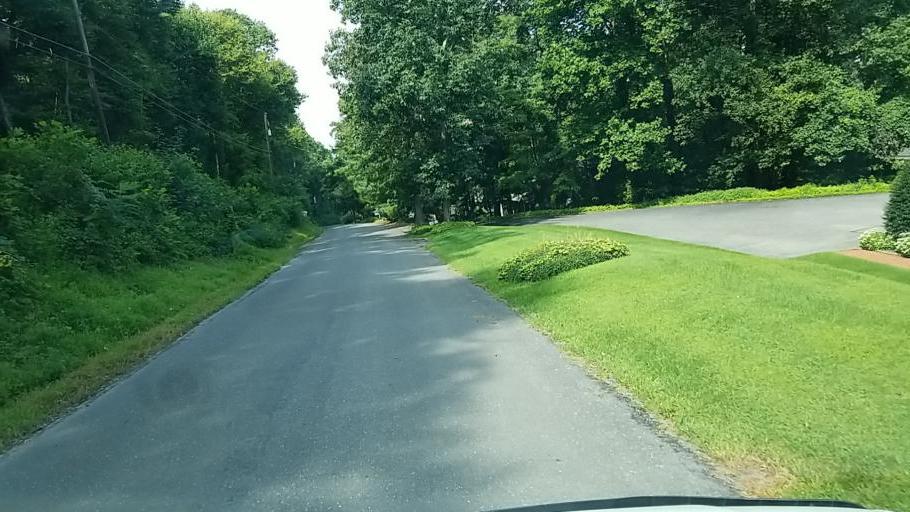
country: US
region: Pennsylvania
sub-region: Dauphin County
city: Millersburg
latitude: 40.5270
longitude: -76.9575
